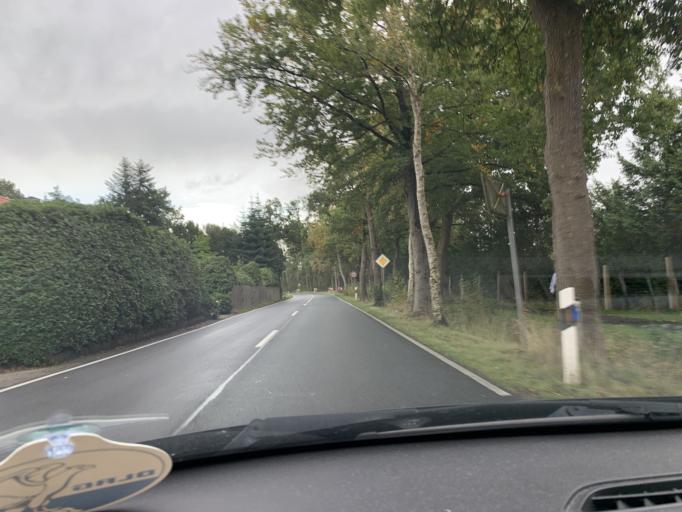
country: DE
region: Lower Saxony
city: Apen
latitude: 53.2287
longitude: 7.7872
